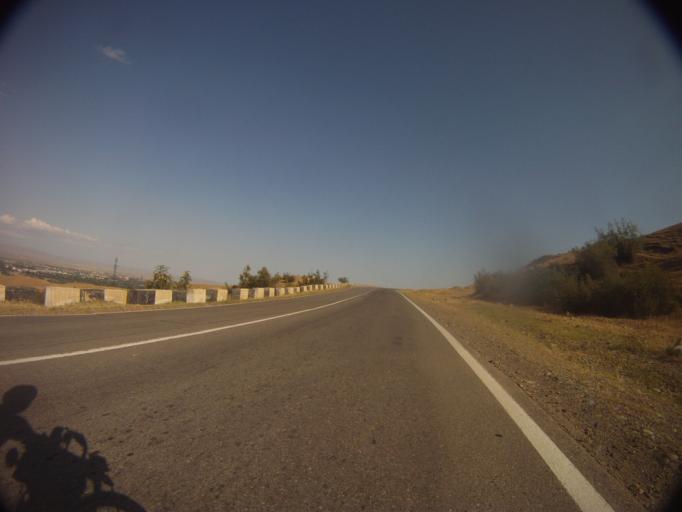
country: GE
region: Kvemo Kartli
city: Rust'avi
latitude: 41.5401
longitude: 44.9767
